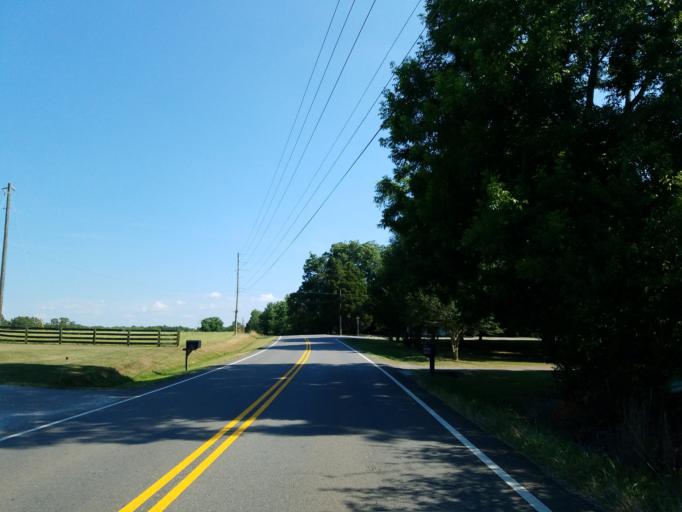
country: US
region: Georgia
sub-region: Fulton County
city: Milton
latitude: 34.2341
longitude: -84.2911
